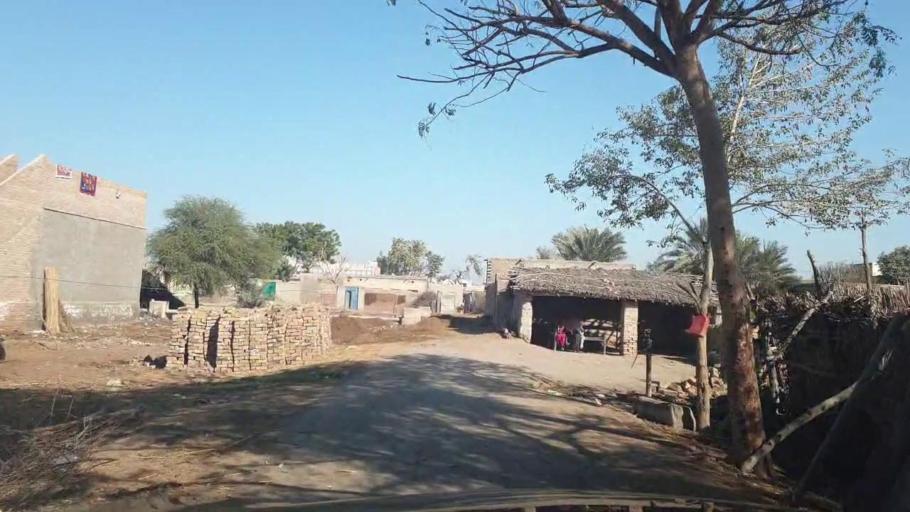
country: PK
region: Sindh
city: Ghotki
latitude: 28.0001
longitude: 69.3429
